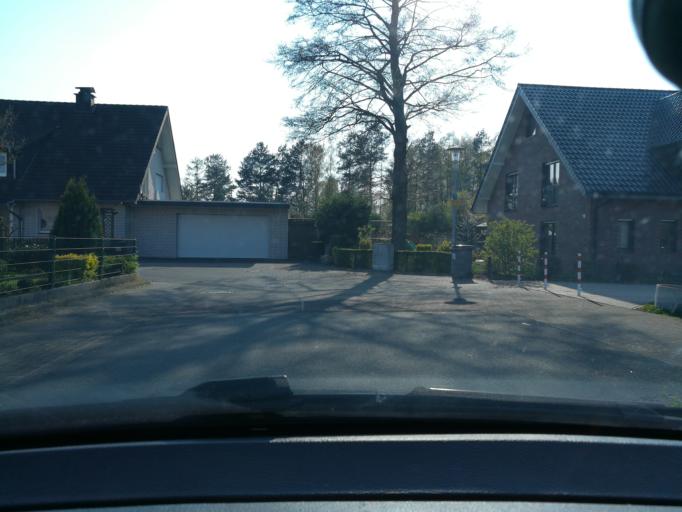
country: DE
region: North Rhine-Westphalia
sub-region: Regierungsbezirk Detmold
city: Oerlinghausen
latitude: 51.9312
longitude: 8.5995
